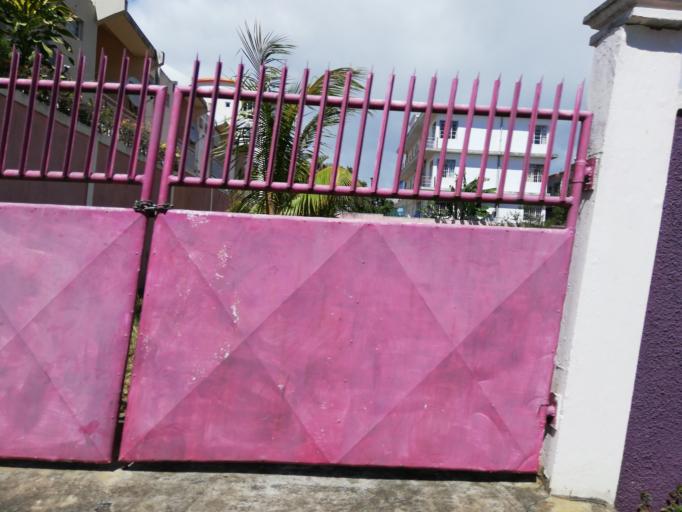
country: MU
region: Plaines Wilhems
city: Ebene
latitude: -20.2295
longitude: 57.4662
